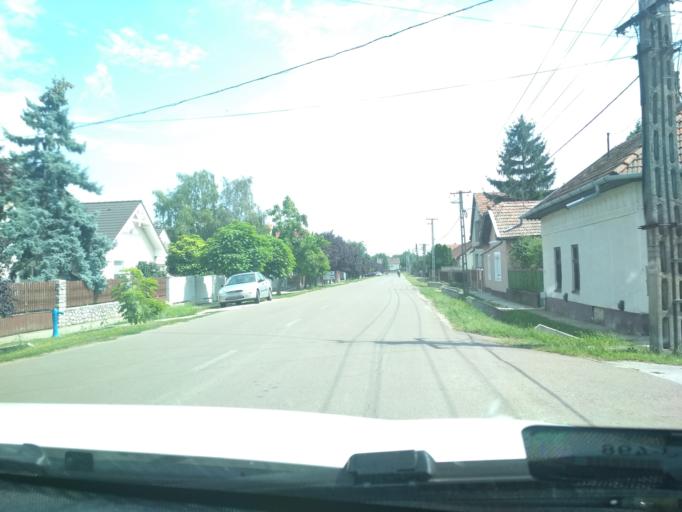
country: HU
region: Jasz-Nagykun-Szolnok
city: Abadszalok
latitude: 47.4768
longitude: 20.5953
